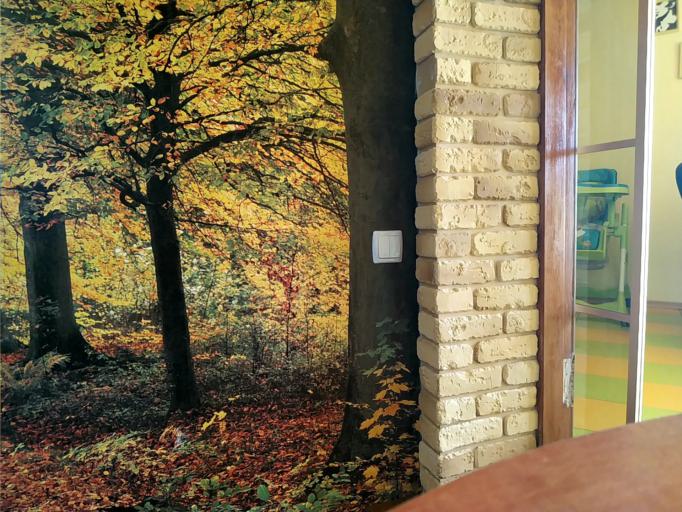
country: RU
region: Moskovskaya
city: Lesnoy
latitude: 56.0628
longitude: 37.9313
